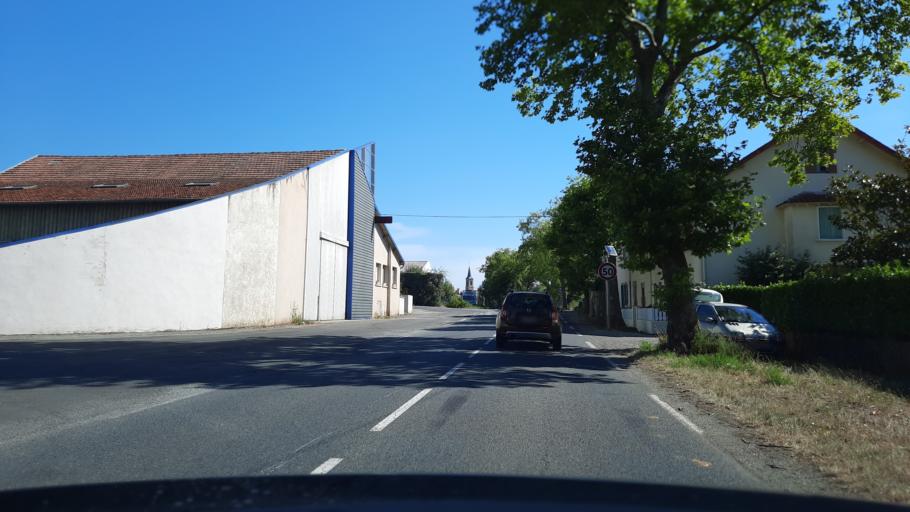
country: FR
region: Midi-Pyrenees
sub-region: Departement du Tarn-et-Garonne
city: Caylus
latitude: 44.3173
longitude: 1.8920
